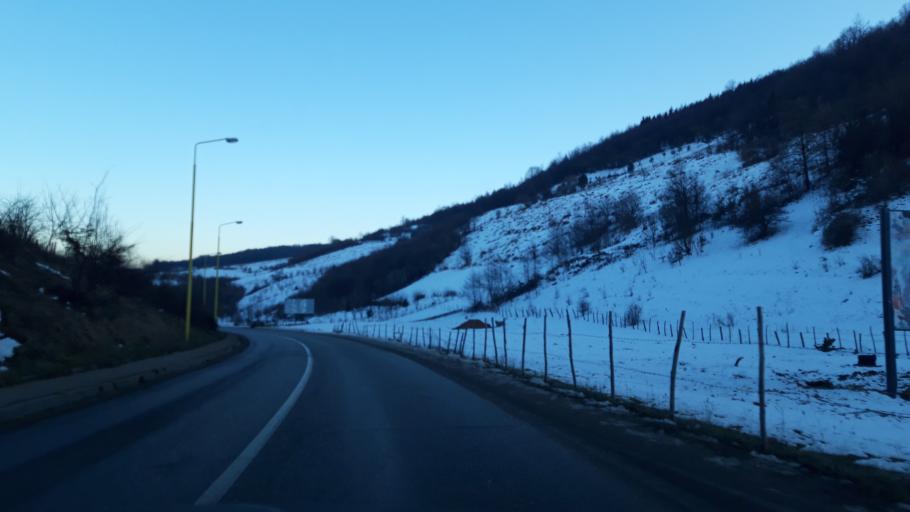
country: BA
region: Republika Srpska
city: Vlasenica
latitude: 44.1806
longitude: 18.9513
